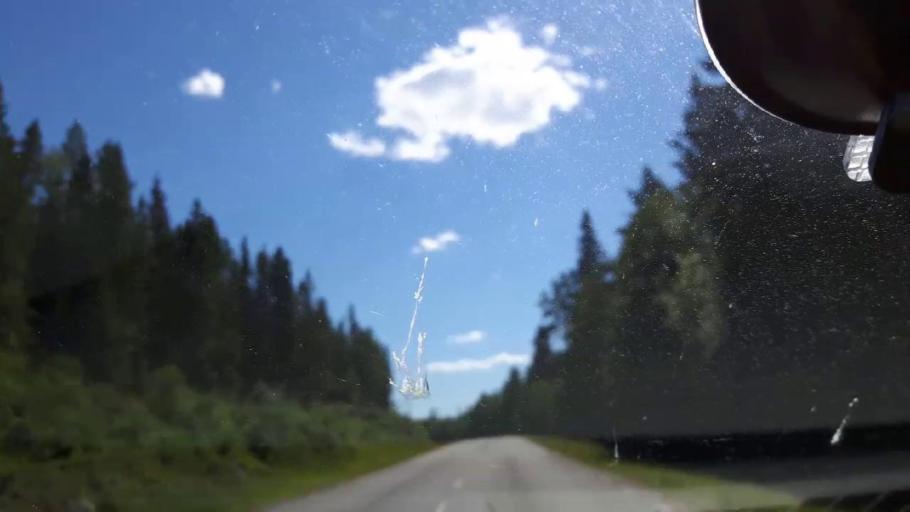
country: SE
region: Vaesternorrland
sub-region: Ange Kommun
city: Fransta
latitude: 62.7241
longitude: 16.3311
